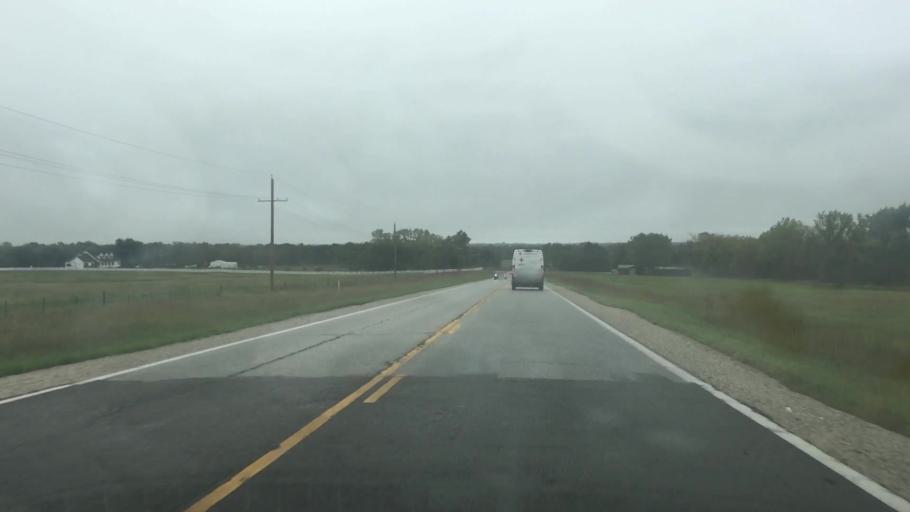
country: US
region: Kansas
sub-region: Anderson County
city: Garnett
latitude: 38.2233
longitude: -95.2485
